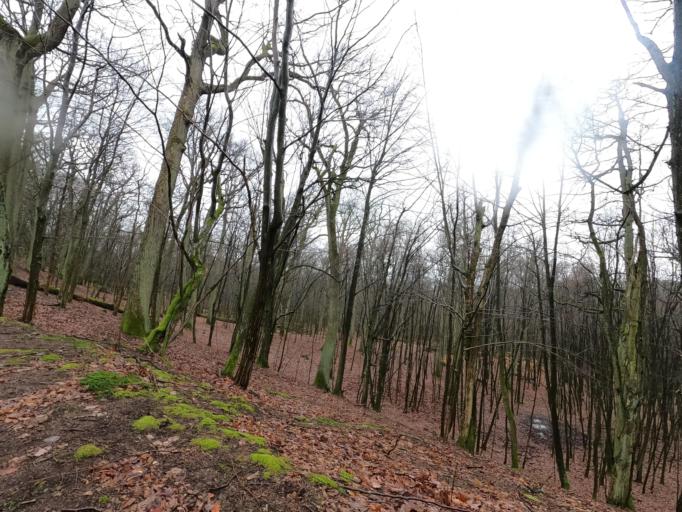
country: PL
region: Greater Poland Voivodeship
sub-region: Powiat pilski
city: Wyrzysk
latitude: 53.1272
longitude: 17.2623
